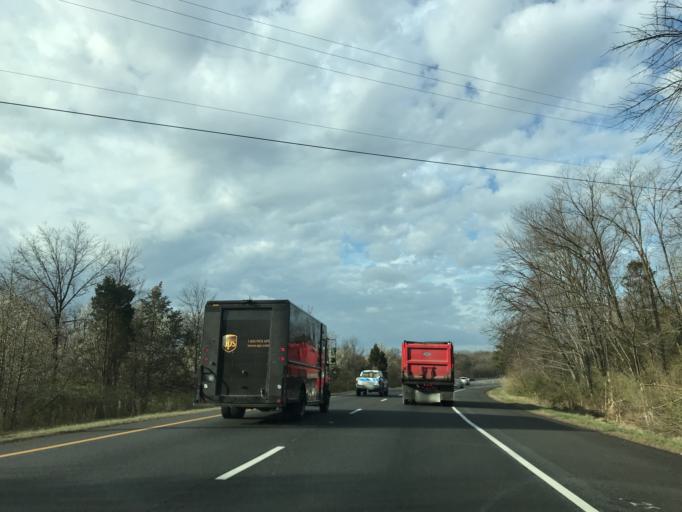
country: US
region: Maryland
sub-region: Montgomery County
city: Hillandale
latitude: 39.0227
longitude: -76.9535
